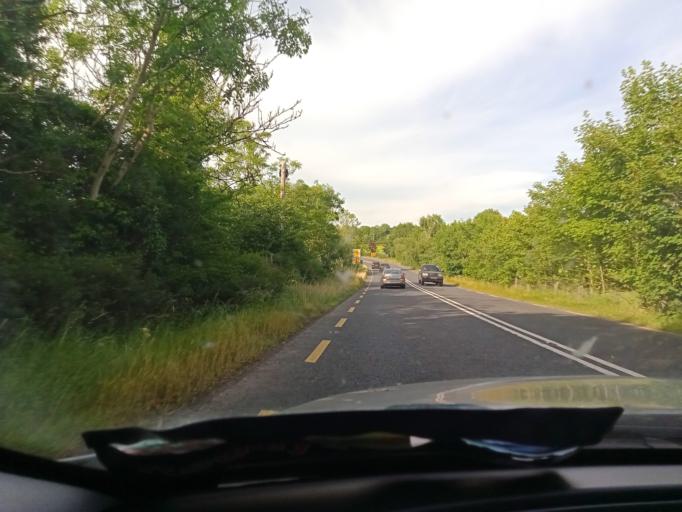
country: IE
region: Ulster
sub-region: An Cabhan
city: Cavan
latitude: 53.9500
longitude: -7.3733
